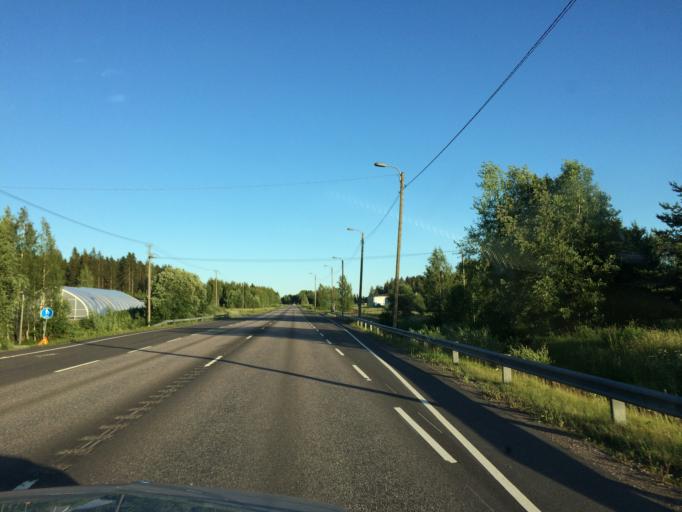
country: FI
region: Haeme
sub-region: Haemeenlinna
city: Tervakoski
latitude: 60.8146
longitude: 24.6438
